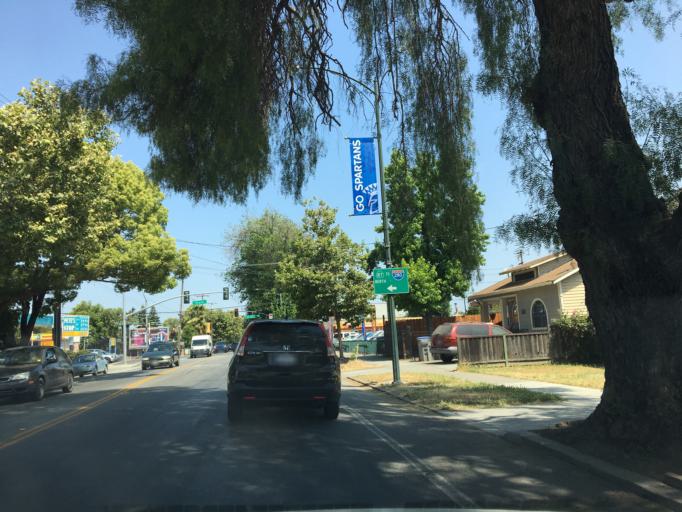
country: US
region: California
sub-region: Santa Clara County
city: San Jose
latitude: 37.3221
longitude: -121.8715
